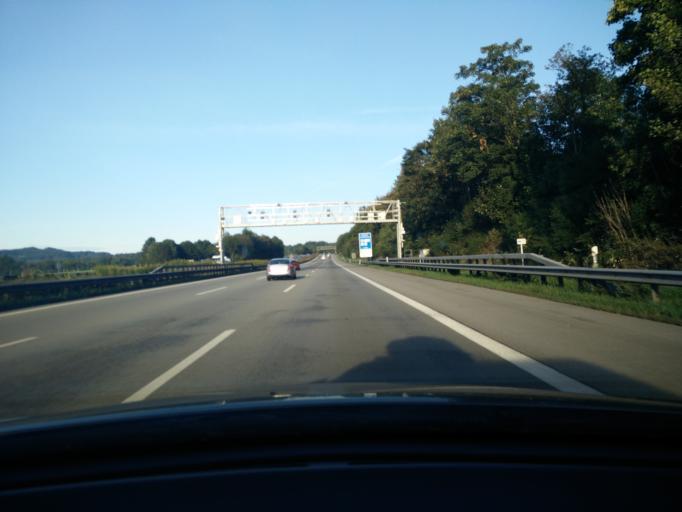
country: DE
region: Bavaria
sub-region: Upper Bavaria
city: Bad Aibling
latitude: 47.8221
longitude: 11.9844
